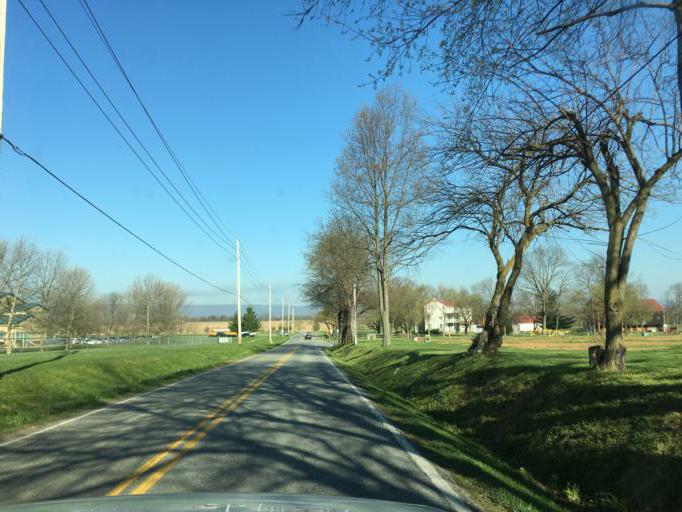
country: US
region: Maryland
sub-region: Frederick County
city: Walkersville
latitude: 39.4964
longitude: -77.3471
